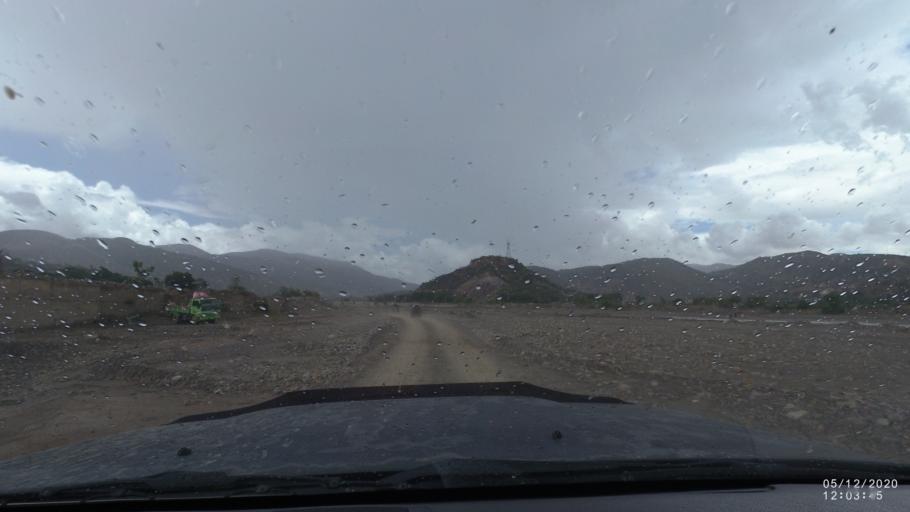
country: BO
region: Cochabamba
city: Sipe Sipe
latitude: -17.5716
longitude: -66.3536
